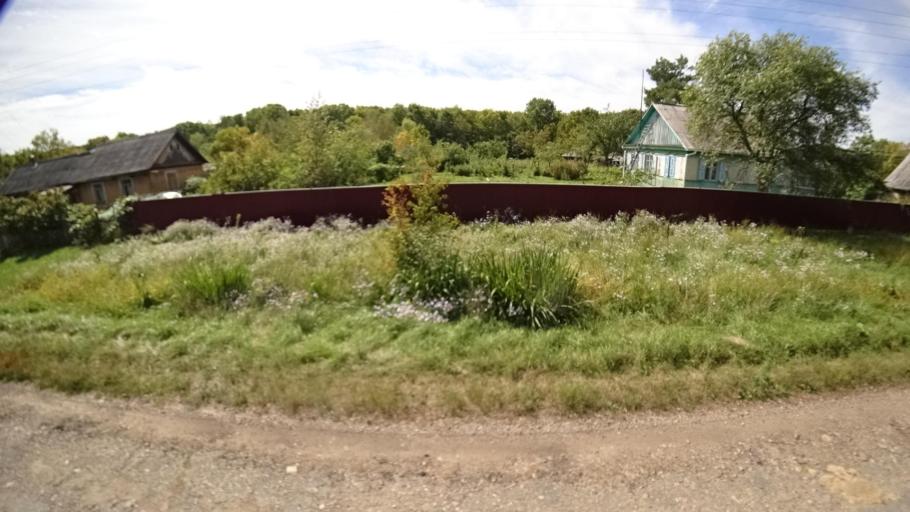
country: RU
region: Primorskiy
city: Yakovlevka
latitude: 44.6544
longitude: 133.7457
